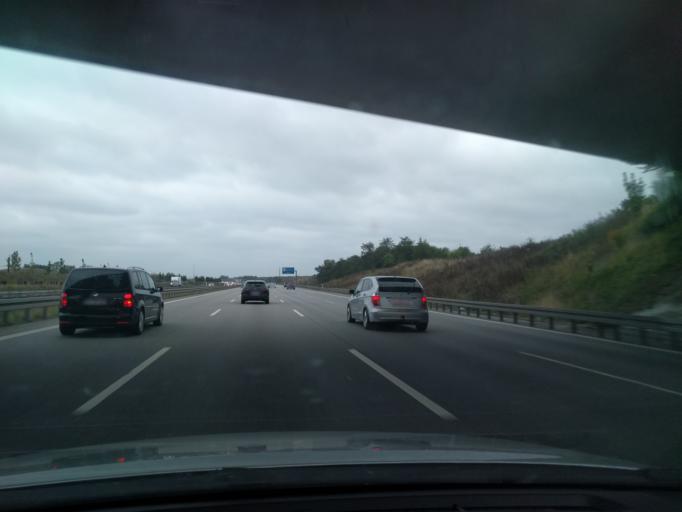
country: DK
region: Zealand
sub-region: Solrod Kommune
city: Solrod Strand
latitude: 55.5720
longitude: 12.2472
